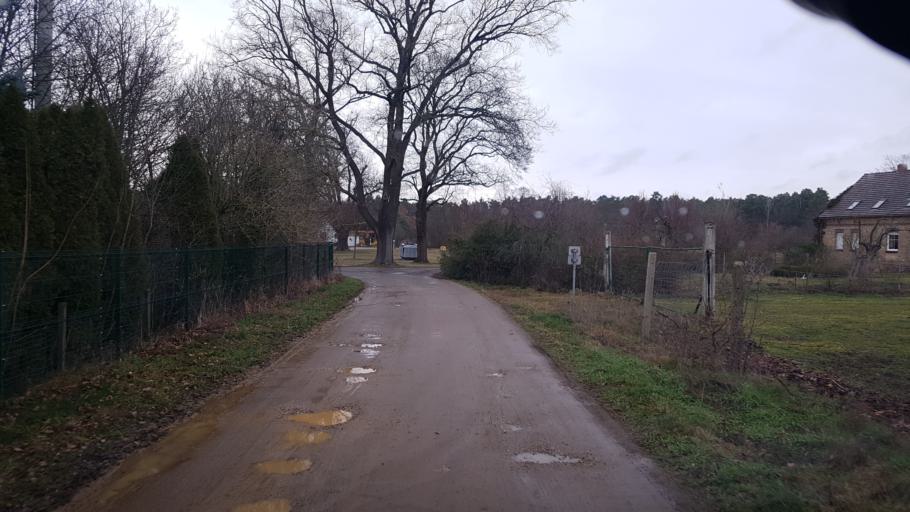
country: DE
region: Brandenburg
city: Sallgast
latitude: 51.6654
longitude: 13.8256
